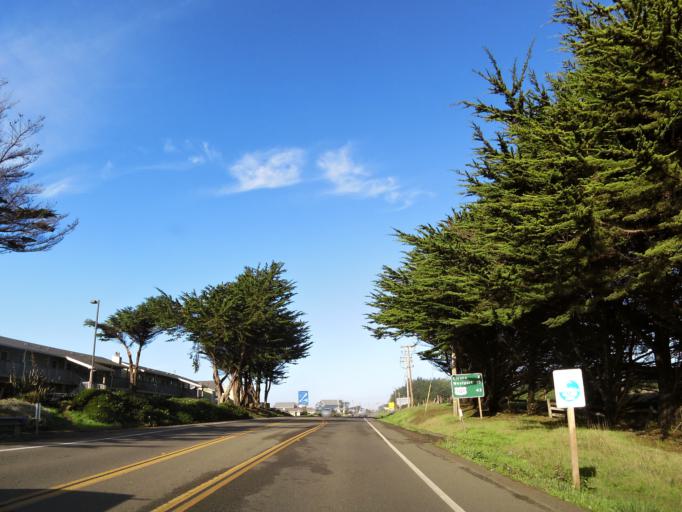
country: US
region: California
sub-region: Mendocino County
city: Fort Bragg
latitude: 39.4594
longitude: -123.8066
